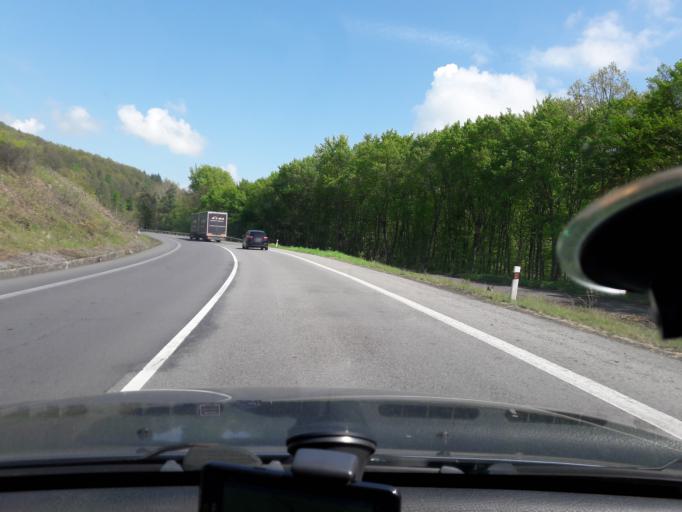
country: SK
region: Banskobystricky
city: Krupina
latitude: 48.3881
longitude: 19.0849
